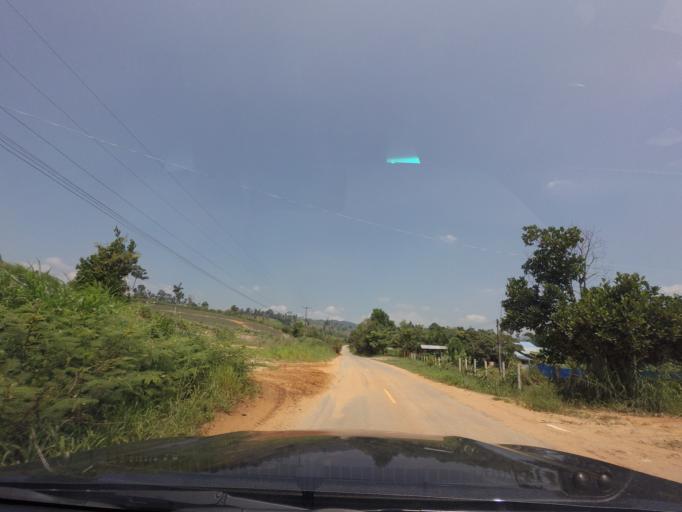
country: TH
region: Loei
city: Na Haeo
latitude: 17.5449
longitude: 100.8788
